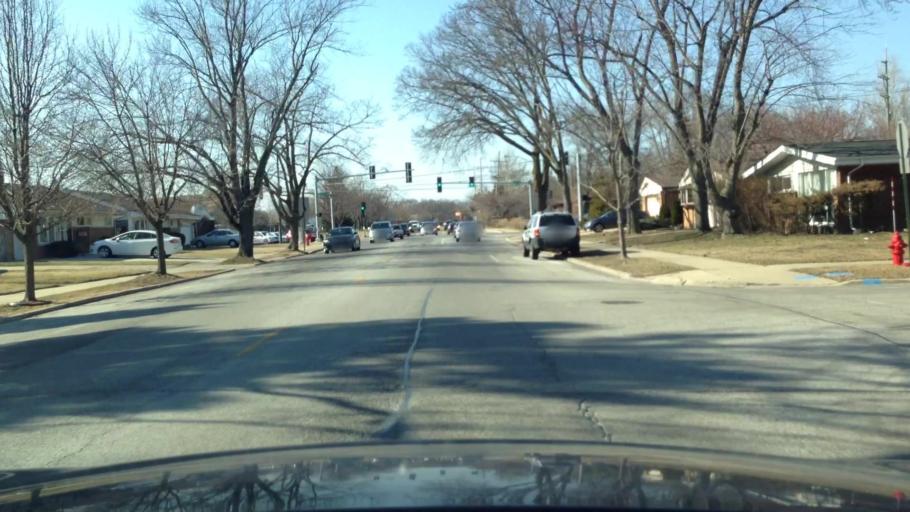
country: US
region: Illinois
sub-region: Cook County
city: Glenview
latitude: 42.0544
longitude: -87.8110
